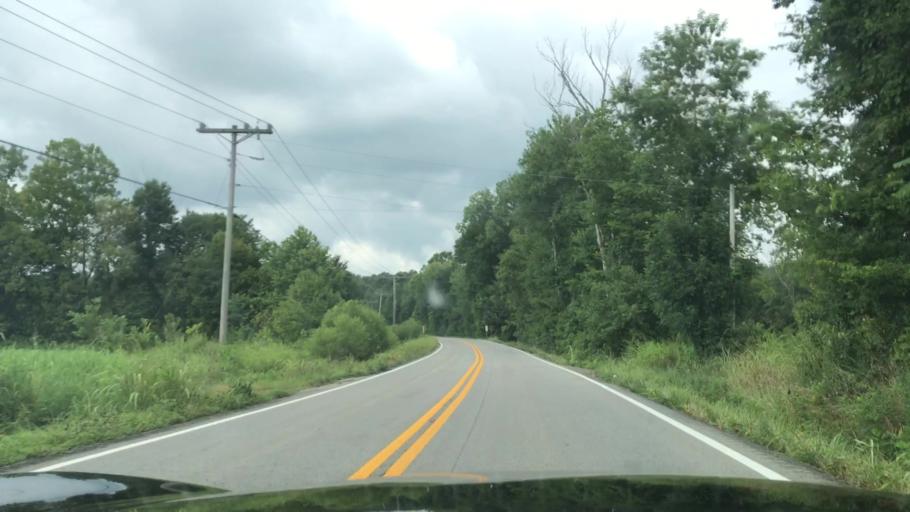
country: US
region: Kentucky
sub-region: Muhlenberg County
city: Central City
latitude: 37.2045
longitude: -87.0194
